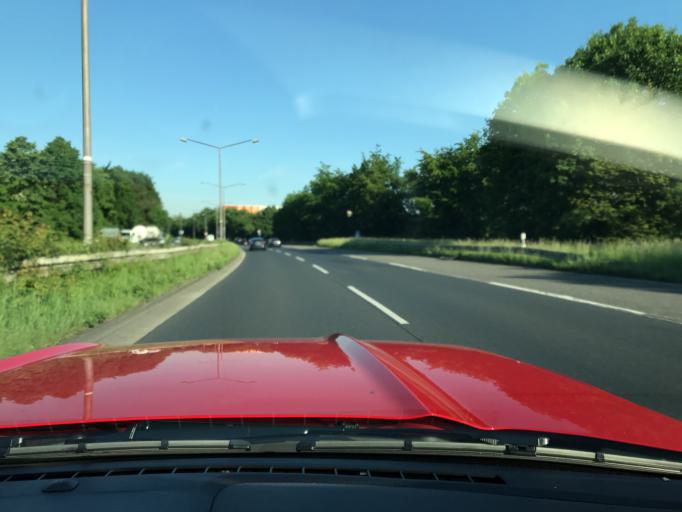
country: DE
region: North Rhine-Westphalia
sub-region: Regierungsbezirk Koln
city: Leverkusen
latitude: 51.0245
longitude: 6.9420
